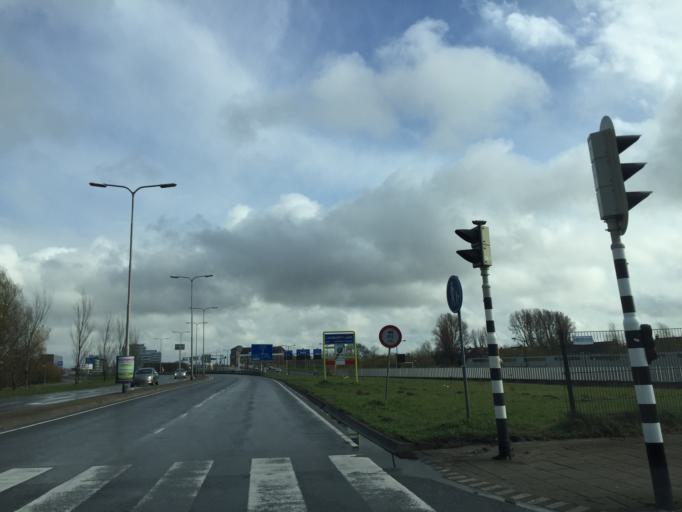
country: NL
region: South Holland
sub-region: Gemeente Leidschendam-Voorburg
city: Voorburg
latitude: 52.0776
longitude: 4.3902
